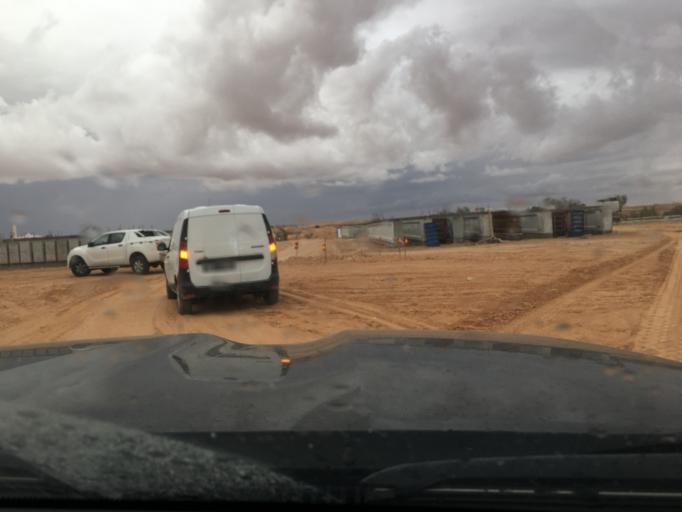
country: TN
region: Madanin
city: Medenine
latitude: 33.3186
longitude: 10.6050
